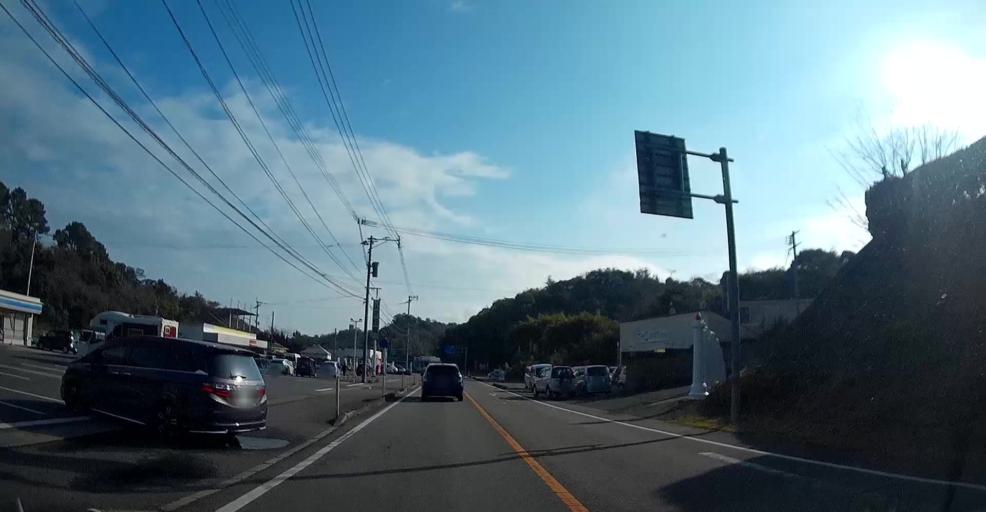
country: JP
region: Kumamoto
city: Yatsushiro
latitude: 32.5550
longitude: 130.4166
